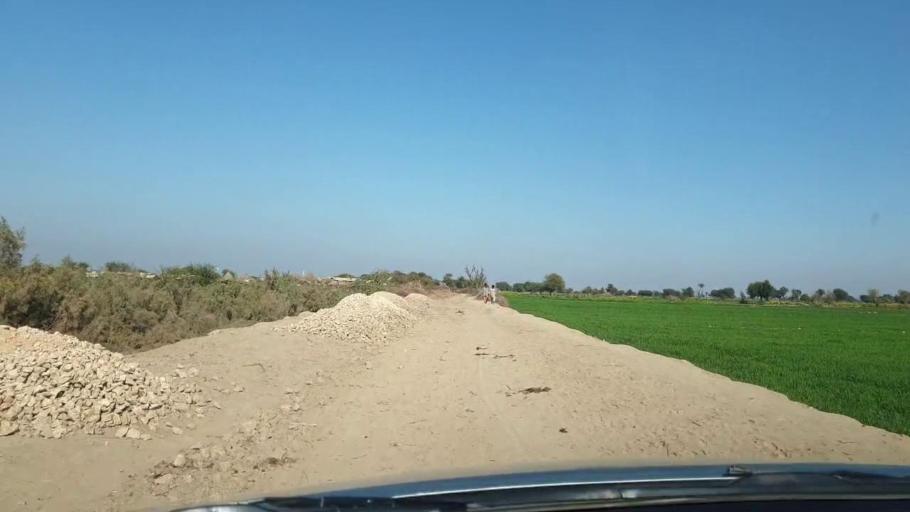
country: PK
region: Sindh
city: Jhol
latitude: 25.9352
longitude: 68.9492
